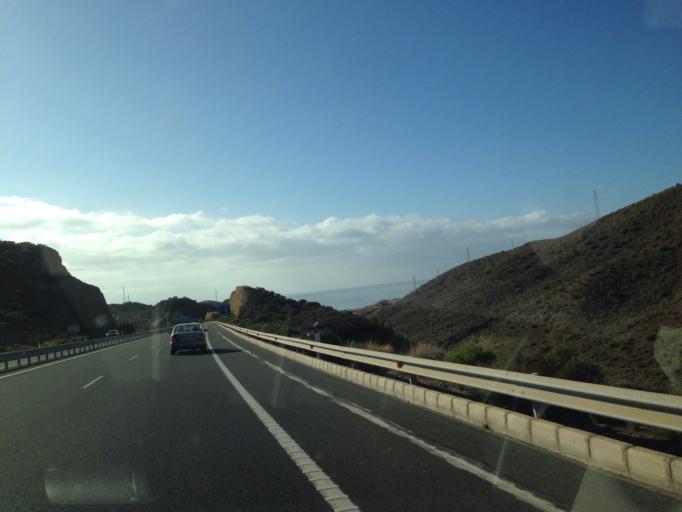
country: ES
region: Canary Islands
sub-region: Provincia de Las Palmas
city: Puerto Rico
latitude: 27.7788
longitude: -15.6770
